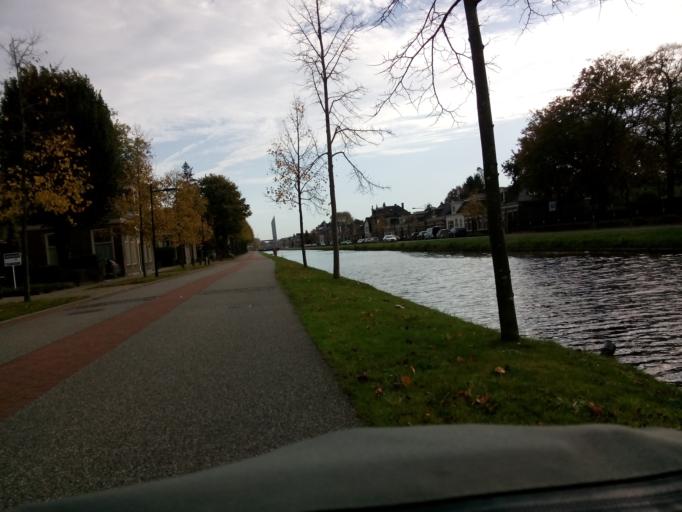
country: NL
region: Drenthe
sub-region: Gemeente Assen
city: Assen
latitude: 52.9943
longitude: 6.5445
